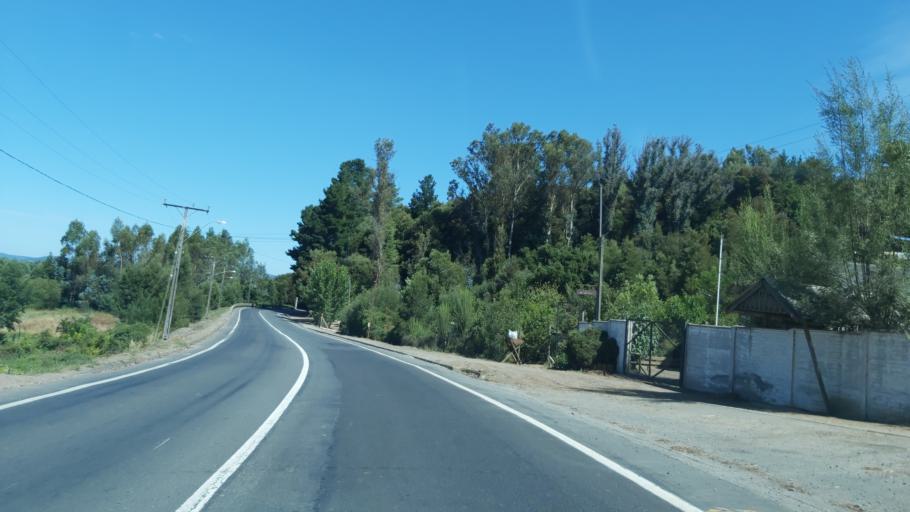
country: CL
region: Biobio
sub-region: Provincia de Concepcion
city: Lota
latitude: -37.1322
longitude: -72.9813
